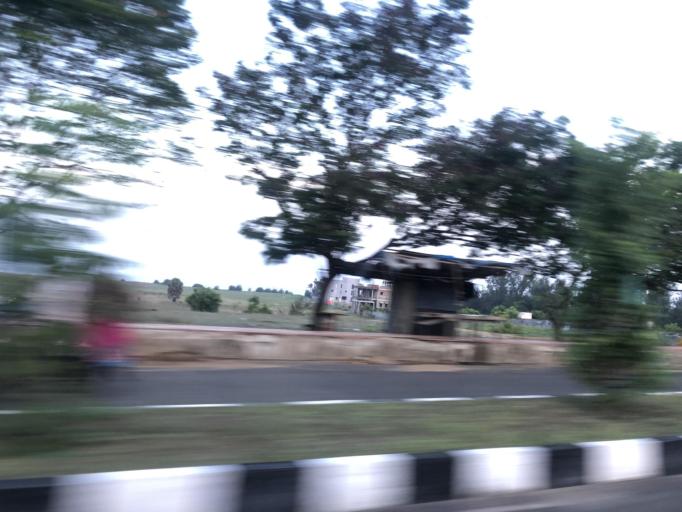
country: IN
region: Tamil Nadu
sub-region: Kancheepuram
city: Mamallapuram
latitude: 12.7499
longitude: 80.2408
